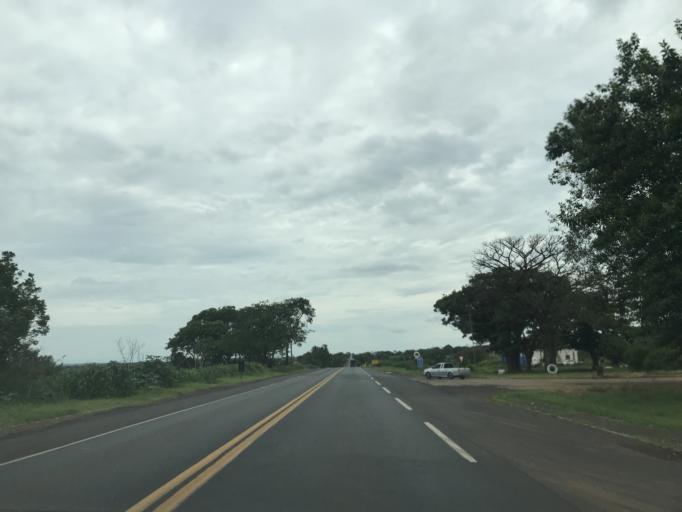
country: BR
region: Minas Gerais
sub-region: Frutal
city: Frutal
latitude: -20.2304
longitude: -49.1535
